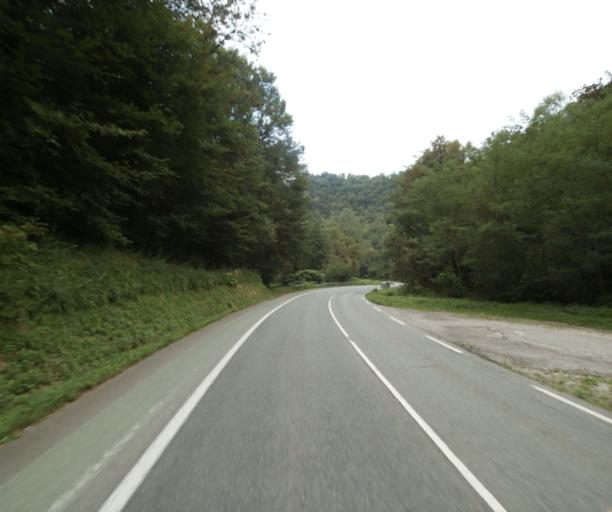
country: FR
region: Rhone-Alpes
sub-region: Departement de l'Isere
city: Gieres
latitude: 45.1665
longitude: 5.7983
